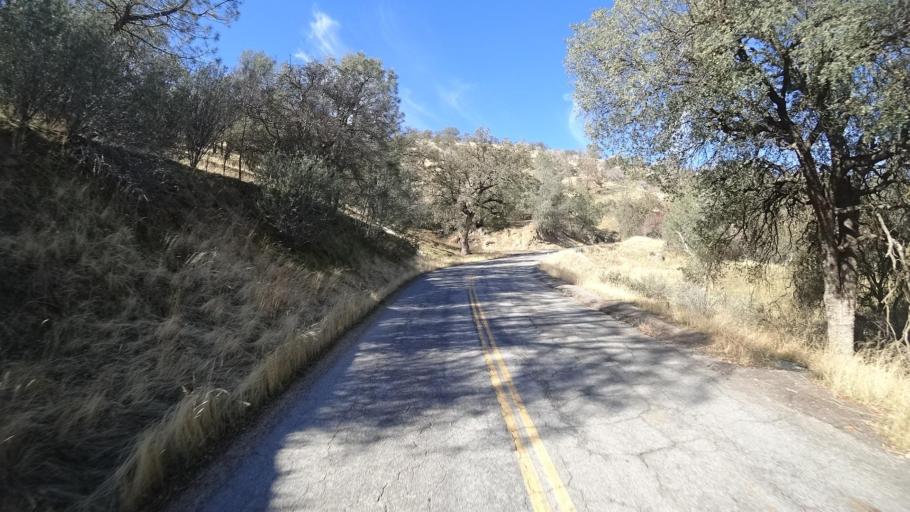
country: US
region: California
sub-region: Kern County
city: Alta Sierra
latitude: 35.6297
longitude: -118.7576
